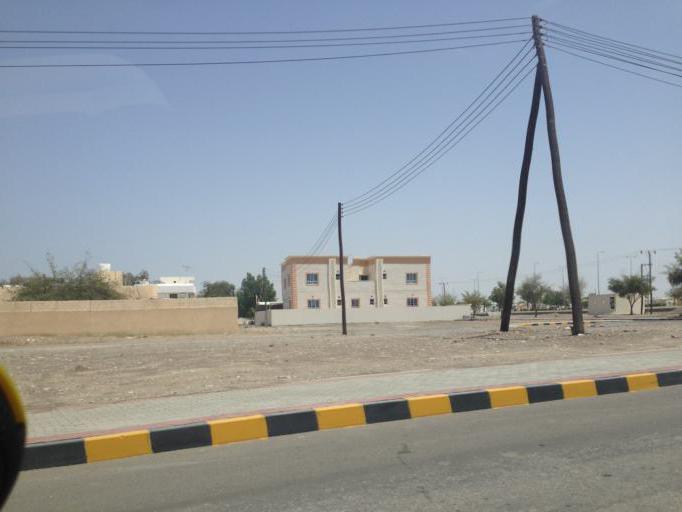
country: OM
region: Muhafazat Masqat
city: As Sib al Jadidah
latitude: 23.6843
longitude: 58.1037
